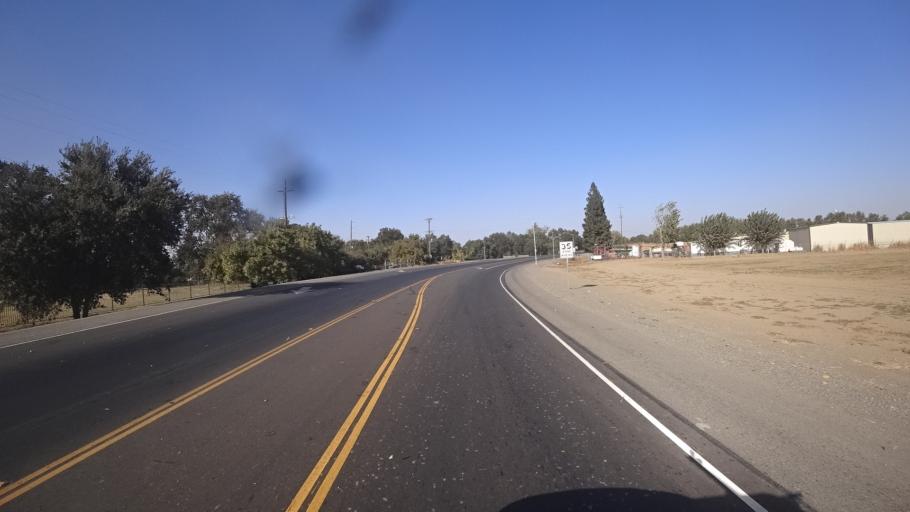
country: US
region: California
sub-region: Yolo County
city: Woodland
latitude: 38.7909
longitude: -121.7280
